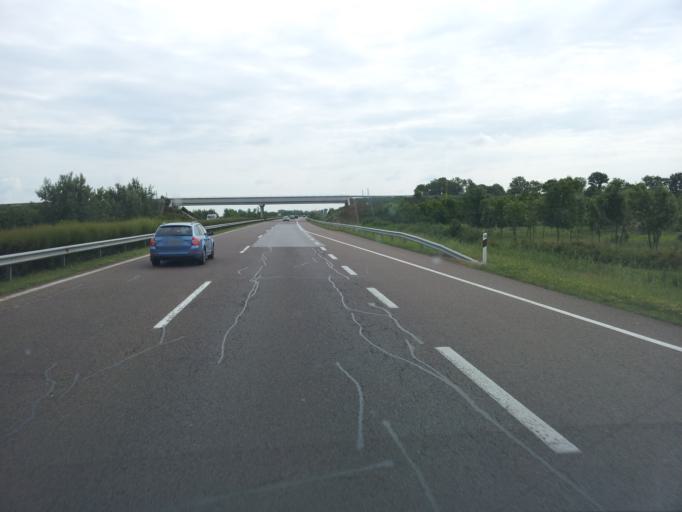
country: HU
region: Heves
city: Szihalom
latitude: 47.7676
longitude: 20.5208
